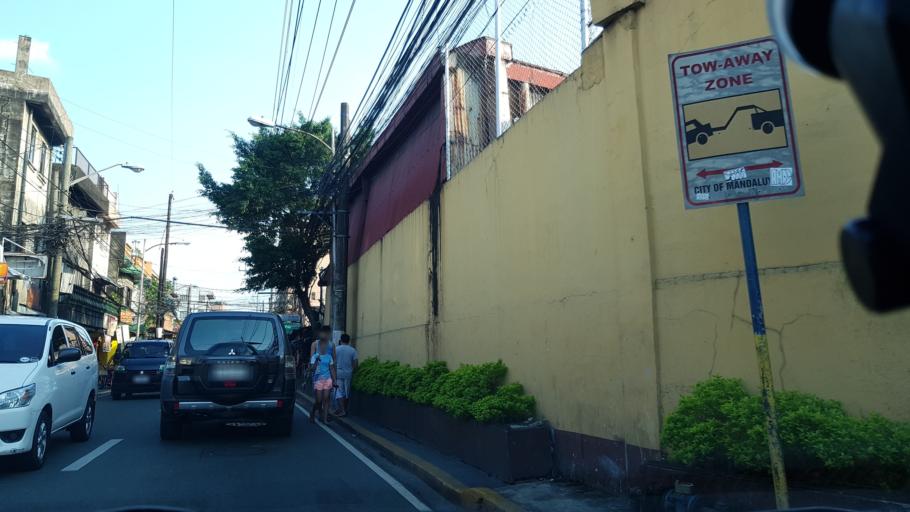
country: PH
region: Metro Manila
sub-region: Mandaluyong
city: Mandaluyong City
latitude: 14.5772
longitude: 121.0270
